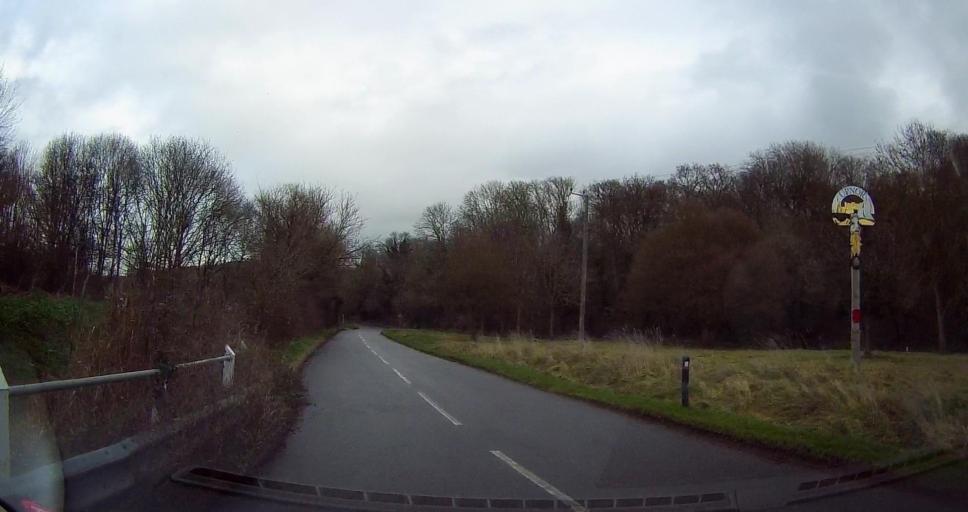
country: GB
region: England
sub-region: Medway
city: Rochester
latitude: 51.4083
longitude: 0.5196
